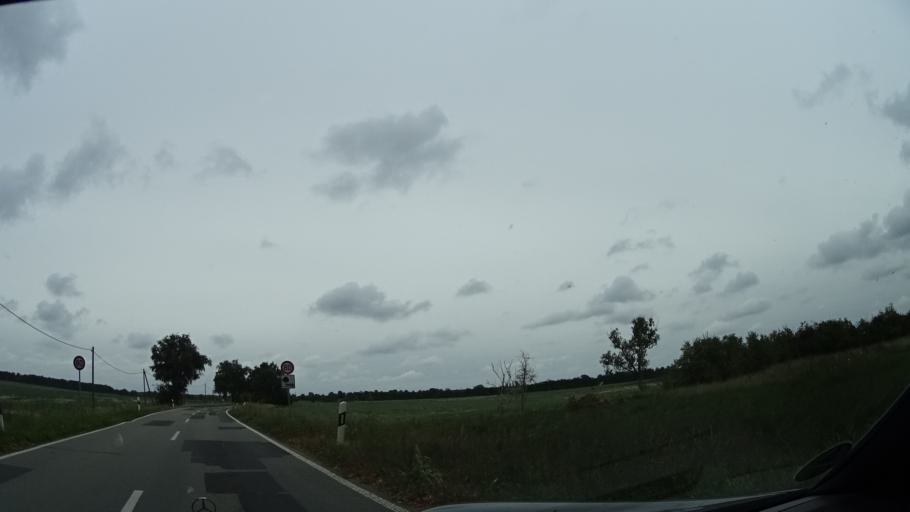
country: DE
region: Brandenburg
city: Walsleben
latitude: 52.9460
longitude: 12.7047
